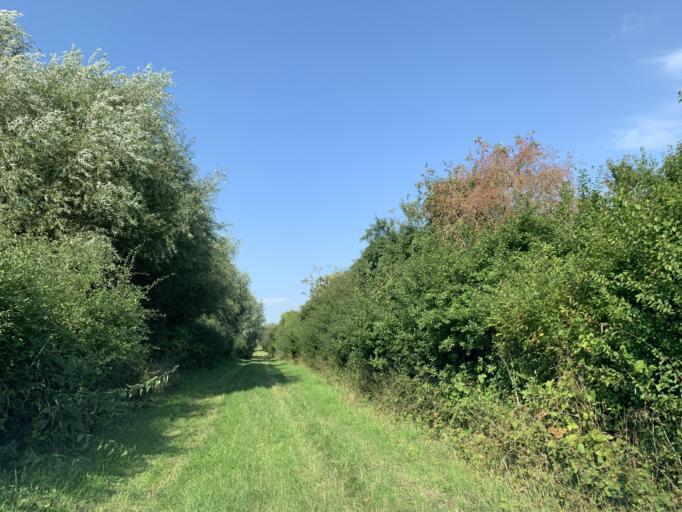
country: DE
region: Mecklenburg-Vorpommern
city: Blankensee
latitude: 53.3949
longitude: 13.2449
